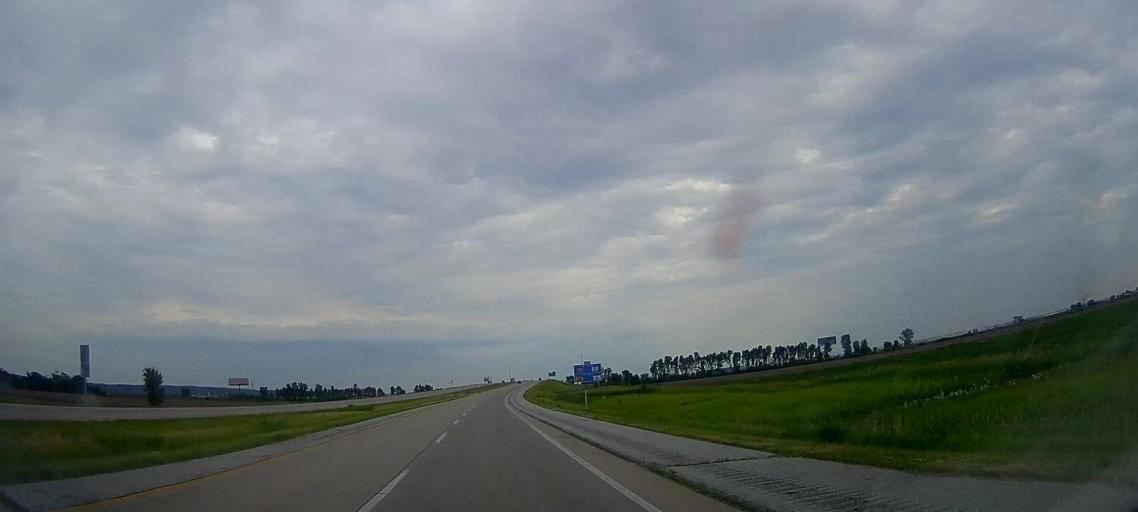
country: US
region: Iowa
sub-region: Harrison County
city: Missouri Valley
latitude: 41.5605
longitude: -95.9174
